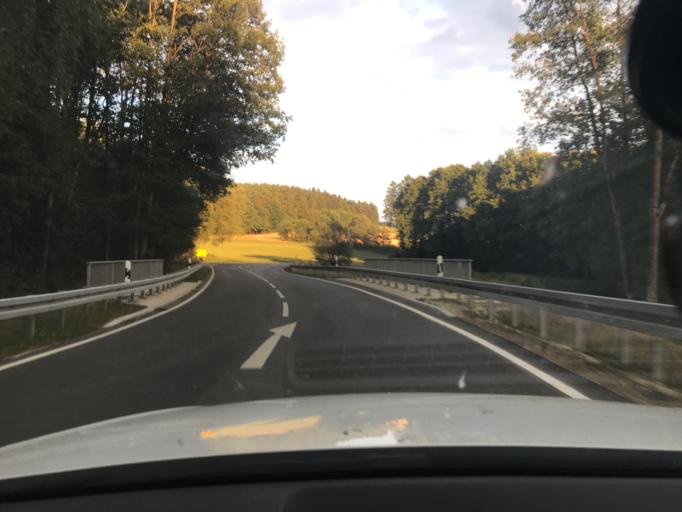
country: DE
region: Bavaria
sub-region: Upper Palatinate
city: Auerbach
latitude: 49.7471
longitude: 11.6050
